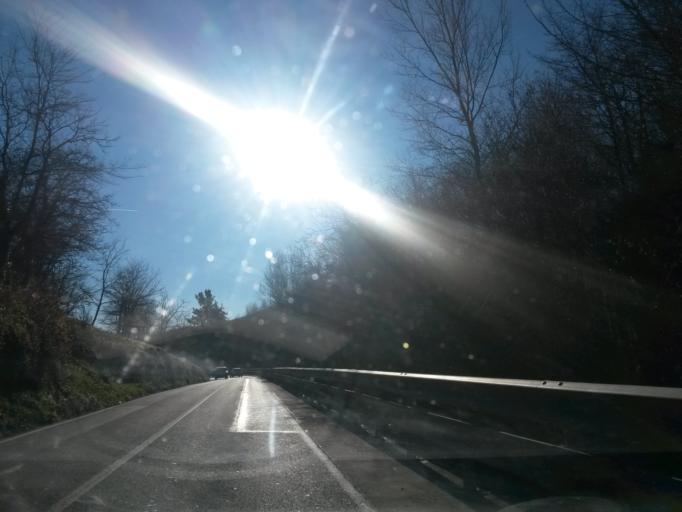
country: ES
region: Catalonia
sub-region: Provincia de Girona
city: Sant Feliu de Pallerols
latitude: 42.0803
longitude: 2.5018
